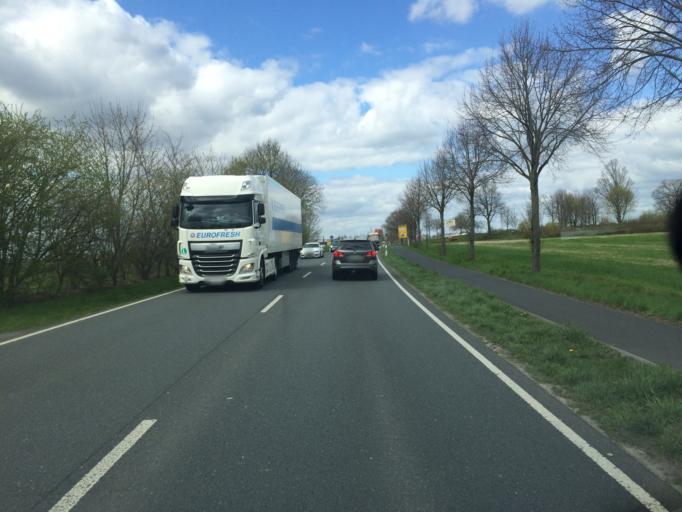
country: DE
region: North Rhine-Westphalia
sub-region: Regierungsbezirk Munster
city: Coesfeld
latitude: 51.9134
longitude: 7.1785
